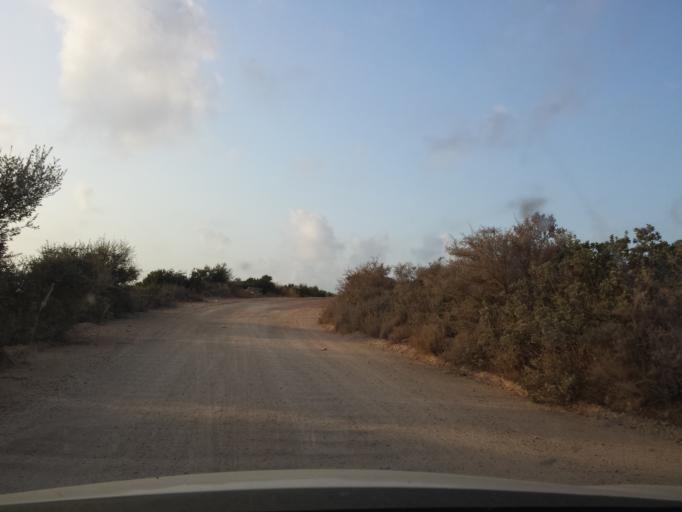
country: GR
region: Peloponnese
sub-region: Nomos Messinias
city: Pylos
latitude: 36.8950
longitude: 21.6915
